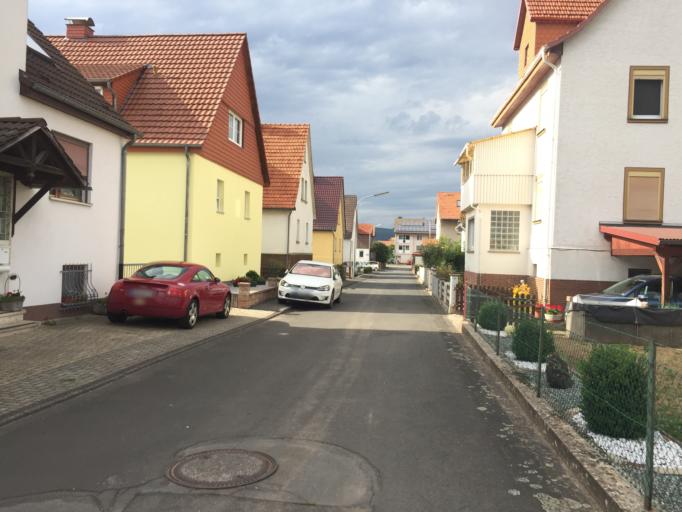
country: DE
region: Hesse
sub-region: Regierungsbezirk Kassel
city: Alheim
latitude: 51.0246
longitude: 9.6730
